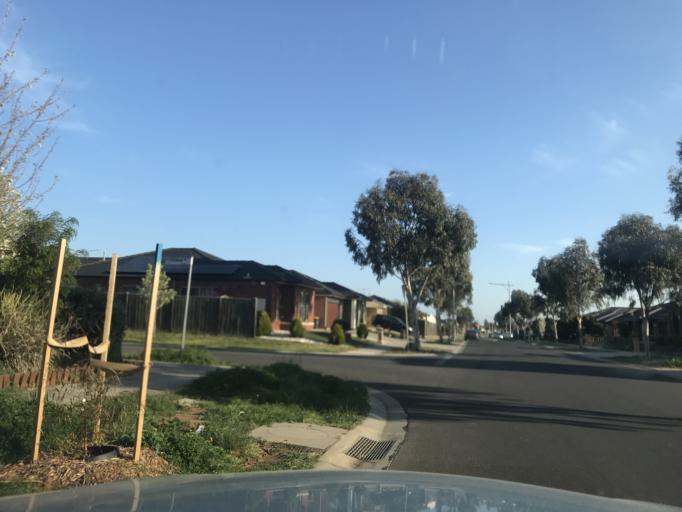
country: AU
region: Victoria
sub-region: Wyndham
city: Williams Landing
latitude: -37.8580
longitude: 144.7231
